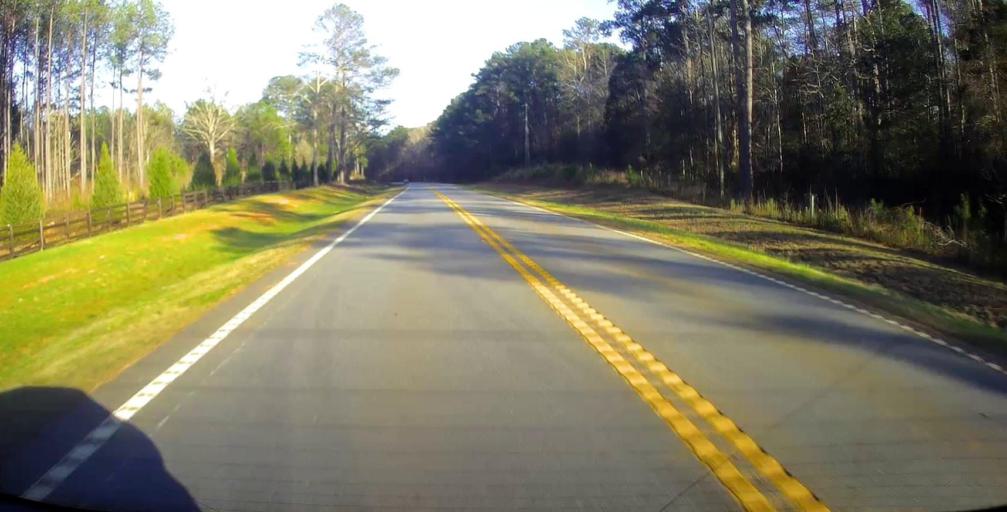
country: US
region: Alabama
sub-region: Chambers County
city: Valley
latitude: 32.7430
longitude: -85.0476
